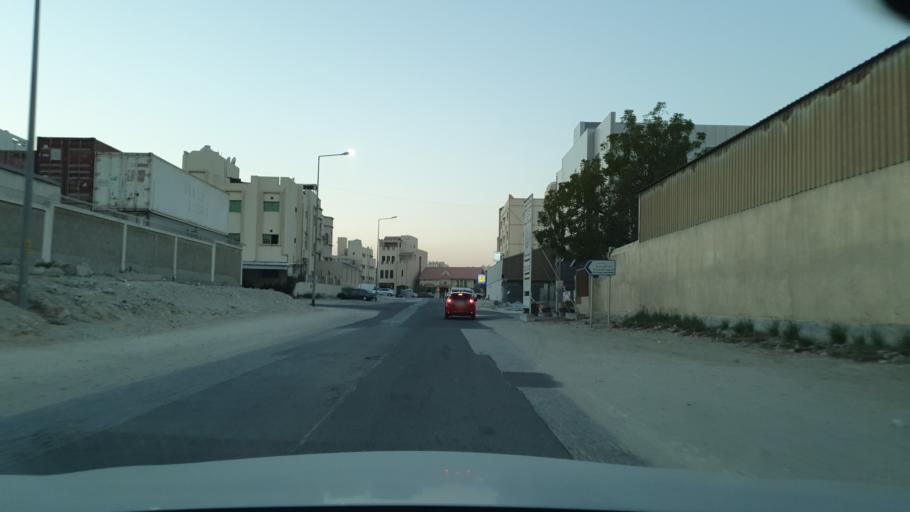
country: BH
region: Northern
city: Ar Rifa'
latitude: 26.1211
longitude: 50.5859
